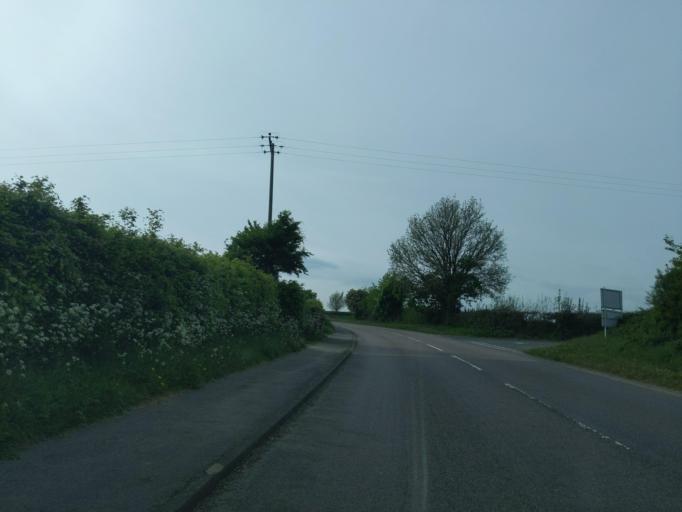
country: GB
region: England
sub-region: Devon
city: Yelverton
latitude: 50.4432
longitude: -4.0877
